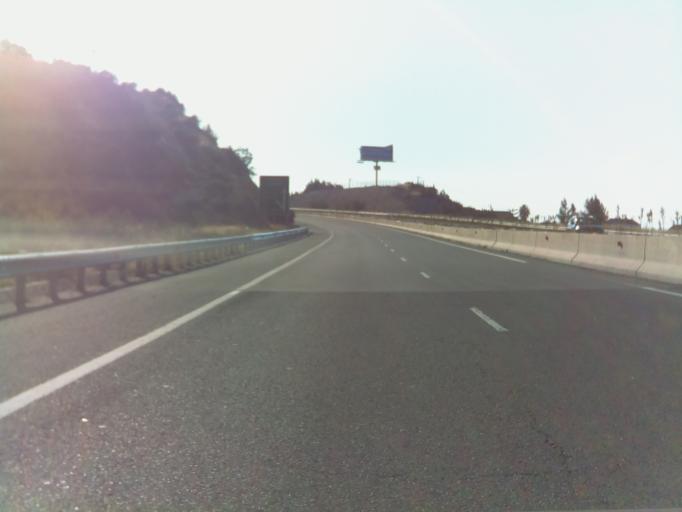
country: CY
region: Limassol
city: Sotira
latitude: 34.6823
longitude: 32.7909
